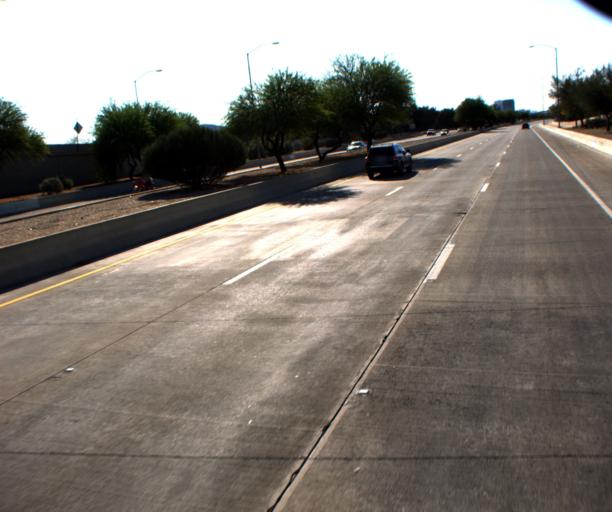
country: US
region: Arizona
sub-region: Pima County
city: South Tucson
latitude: 32.2129
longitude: -110.9506
